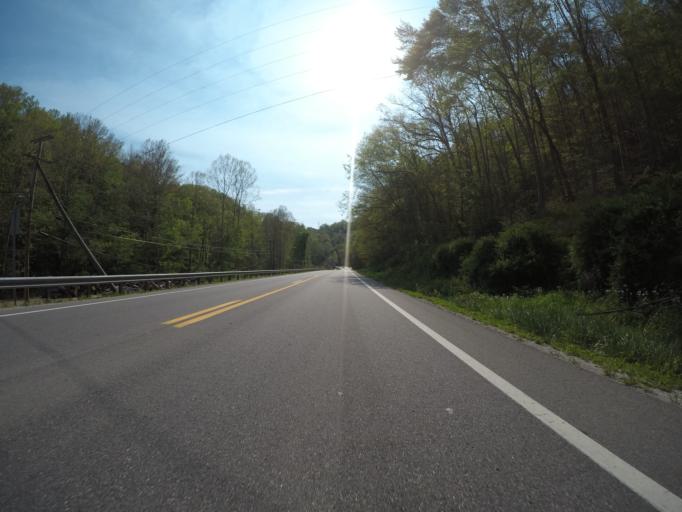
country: US
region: West Virginia
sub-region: Kanawha County
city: Charleston
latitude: 38.3599
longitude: -81.5891
